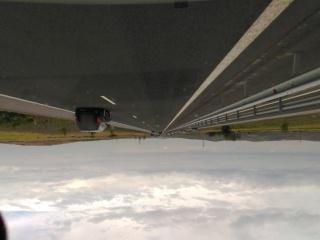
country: BG
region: Sliven
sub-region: Obshtina Sliven
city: Kermen
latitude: 42.4984
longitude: 26.2882
